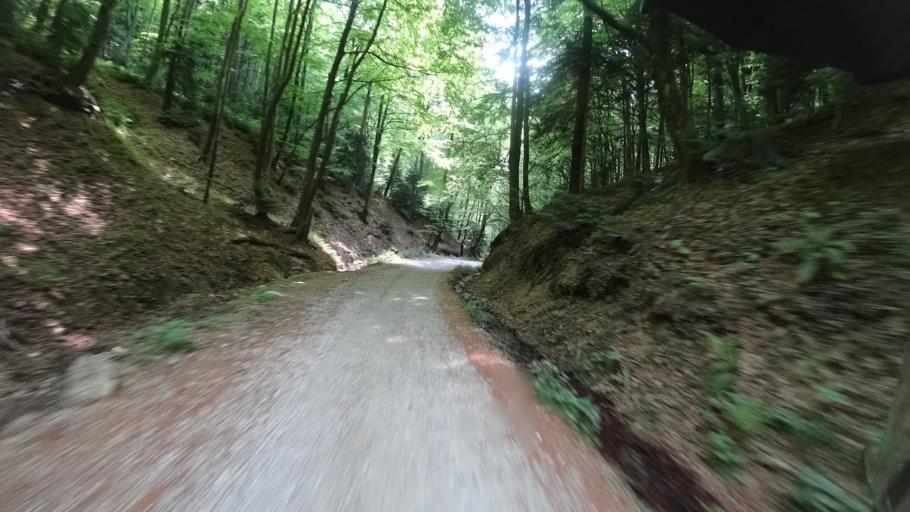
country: HR
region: Grad Zagreb
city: Kasina
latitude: 45.9257
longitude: 16.0238
